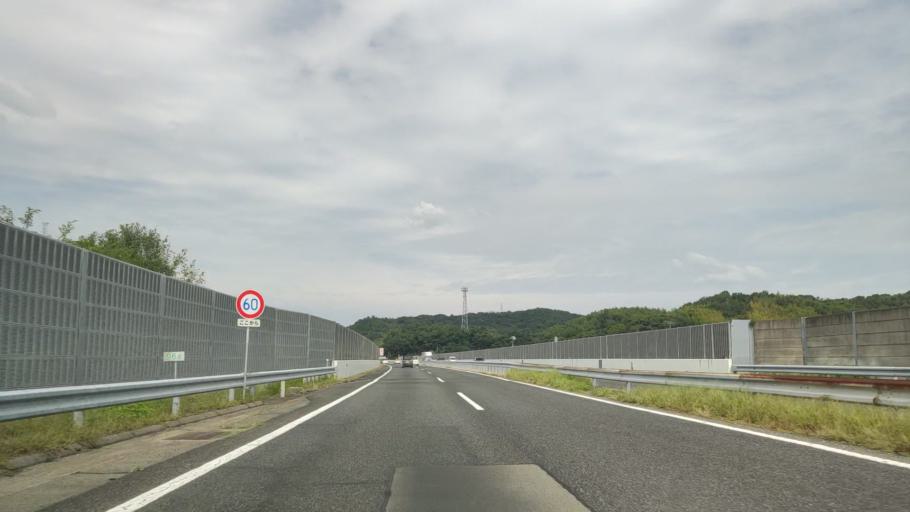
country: JP
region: Wakayama
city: Kainan
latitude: 34.1711
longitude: 135.2351
